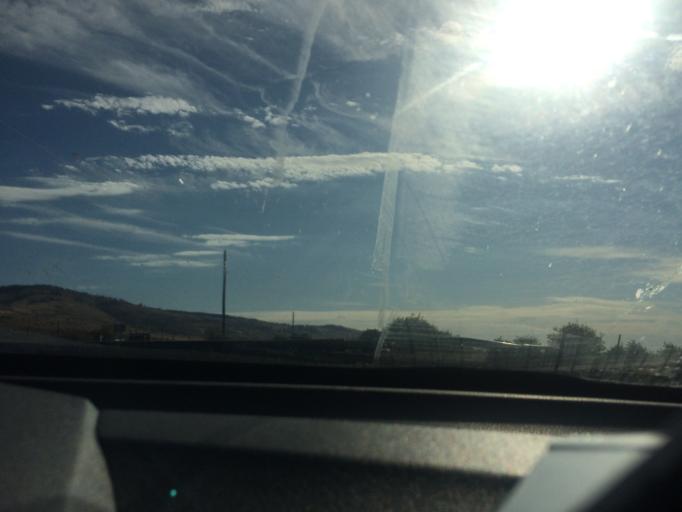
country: US
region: Washington
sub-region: Kittitas County
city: Ellensburg
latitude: 47.1464
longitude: -120.6172
